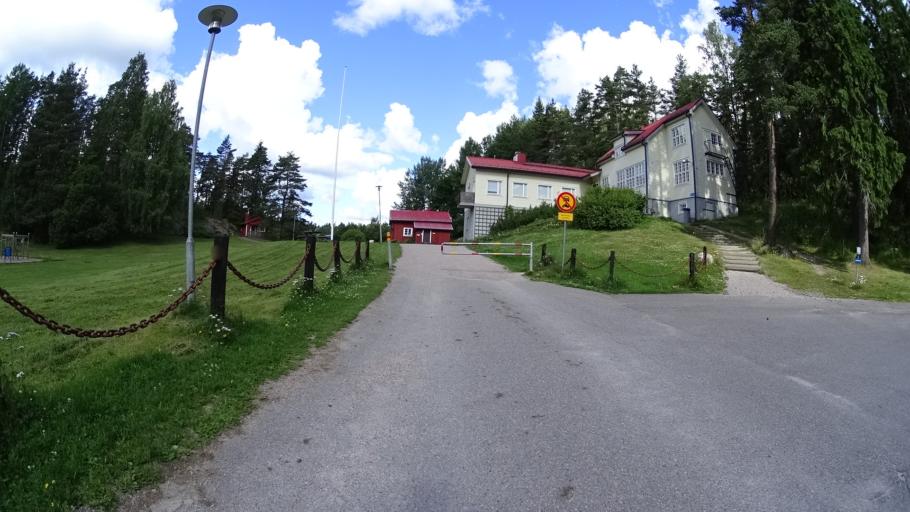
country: FI
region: Uusimaa
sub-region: Helsinki
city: Espoo
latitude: 60.2697
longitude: 24.6508
